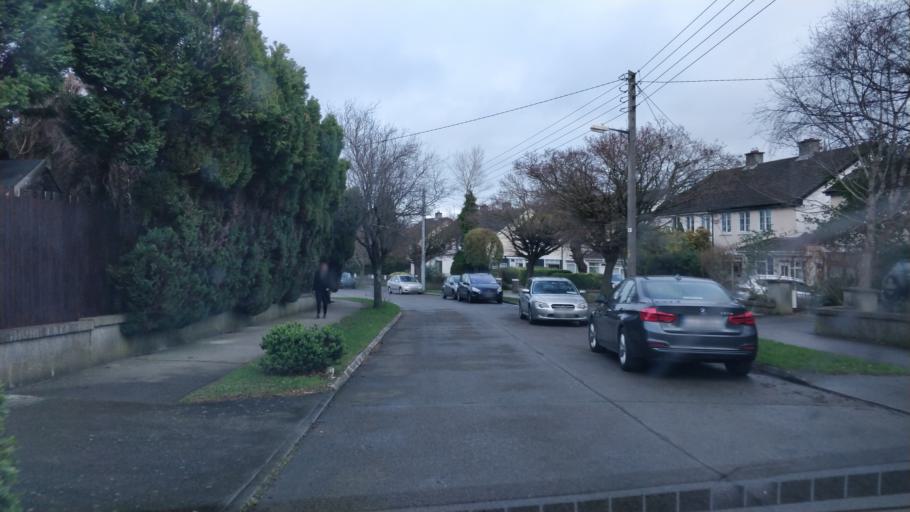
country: IE
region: Leinster
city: Foxrock
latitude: 53.2801
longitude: -6.1728
